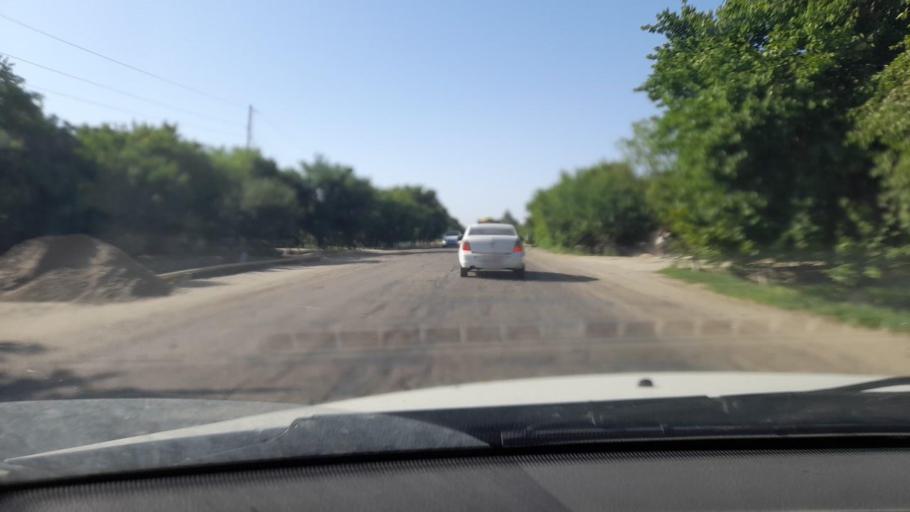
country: UZ
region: Bukhara
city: Romiton
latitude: 40.0607
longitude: 64.3275
